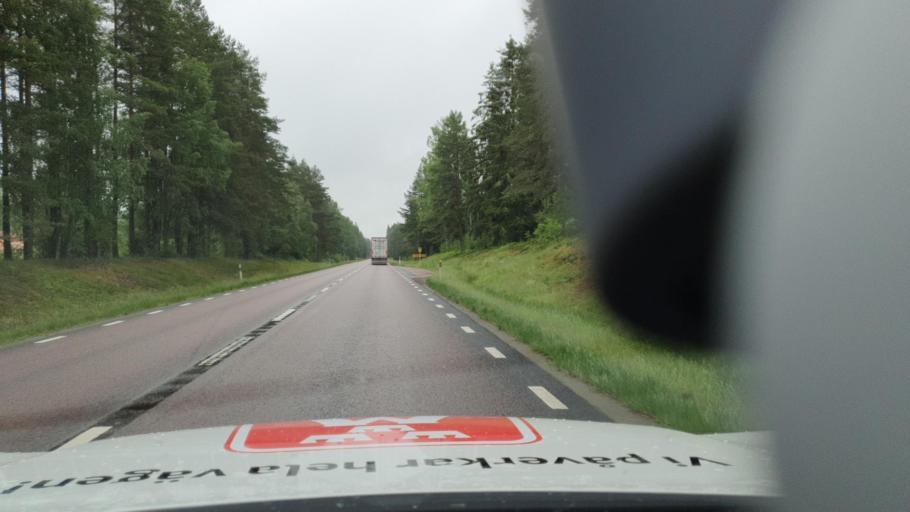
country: SE
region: Vaermland
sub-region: Kristinehamns Kommun
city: Bjorneborg
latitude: 59.2324
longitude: 14.1803
